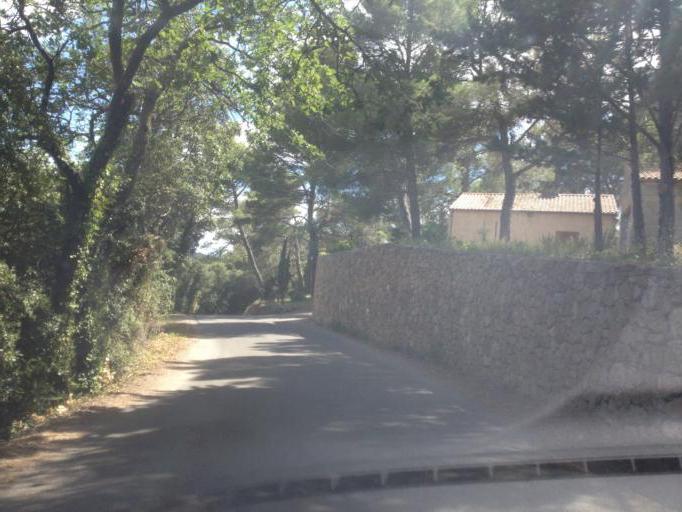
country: FR
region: Provence-Alpes-Cote d'Azur
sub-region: Departement du Vaucluse
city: Malaucene
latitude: 44.1501
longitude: 5.1018
